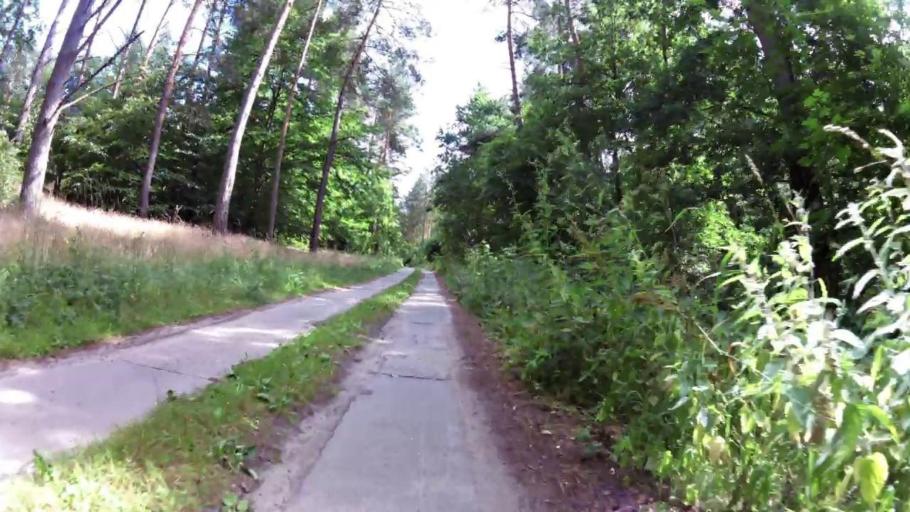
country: PL
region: West Pomeranian Voivodeship
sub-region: Powiat lobeski
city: Lobez
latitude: 53.6410
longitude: 15.5826
